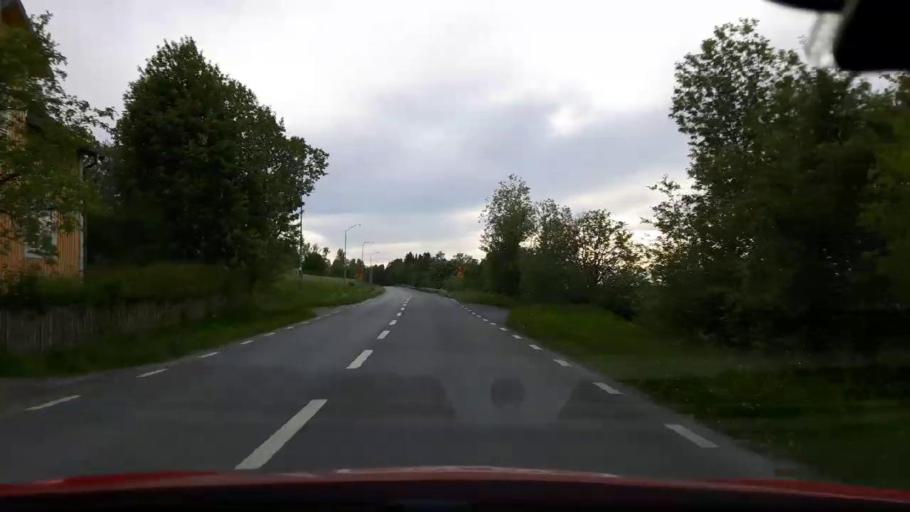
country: SE
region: Jaemtland
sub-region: OEstersunds Kommun
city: Ostersund
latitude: 63.1549
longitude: 14.5227
